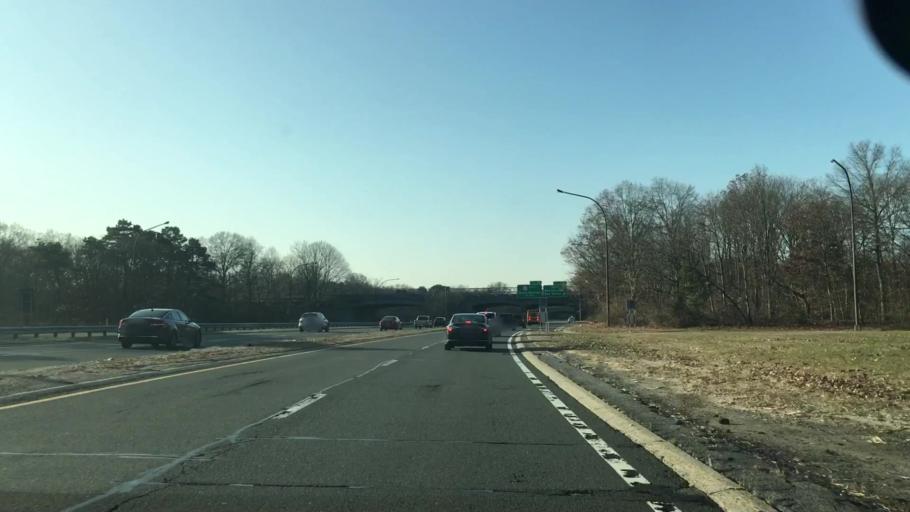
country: US
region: New York
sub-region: Suffolk County
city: Bay Wood
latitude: 40.7393
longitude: -73.2838
